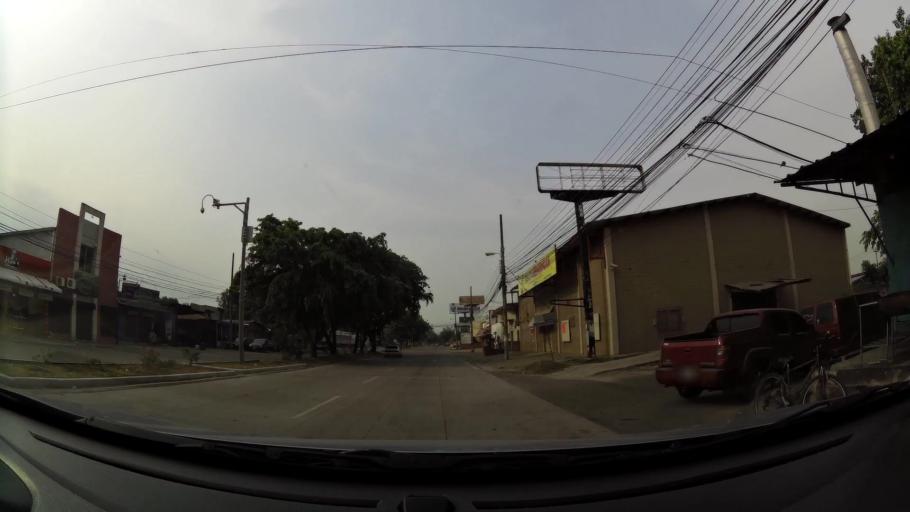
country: HN
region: Cortes
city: San Pedro Sula
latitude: 15.5150
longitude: -88.0176
